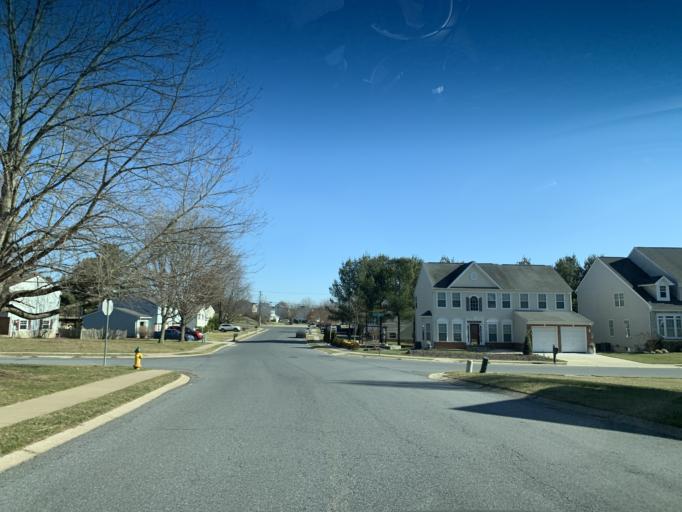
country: US
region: Maryland
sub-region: Carroll County
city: Westminster
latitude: 39.5946
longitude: -76.9913
